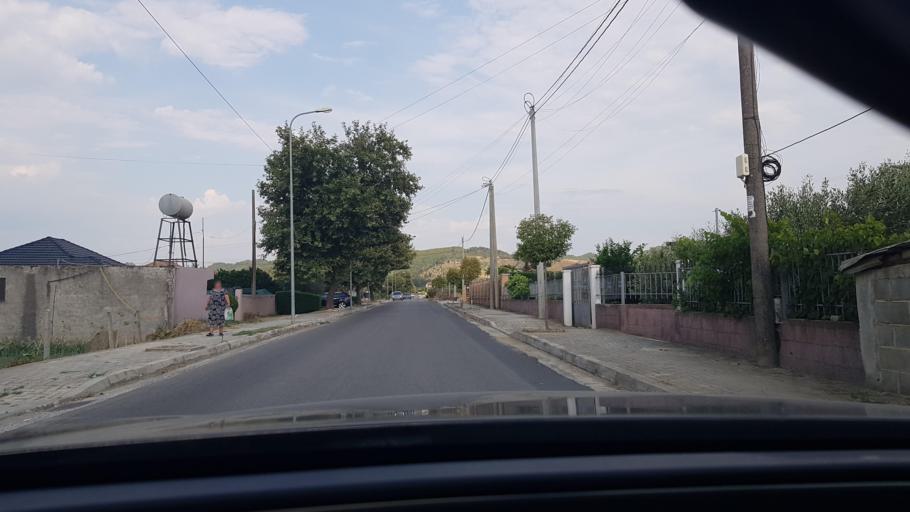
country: AL
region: Durres
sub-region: Rrethi i Durresit
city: Manze
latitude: 41.4744
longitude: 19.5533
